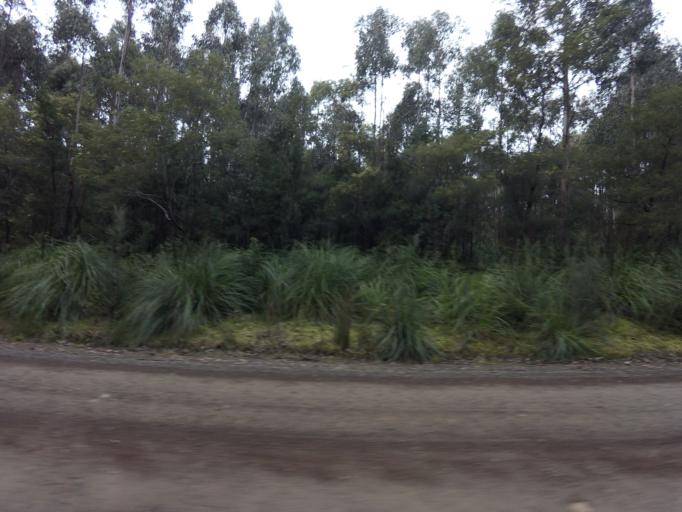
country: AU
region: Tasmania
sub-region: Huon Valley
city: Geeveston
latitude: -43.4703
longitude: 146.8924
